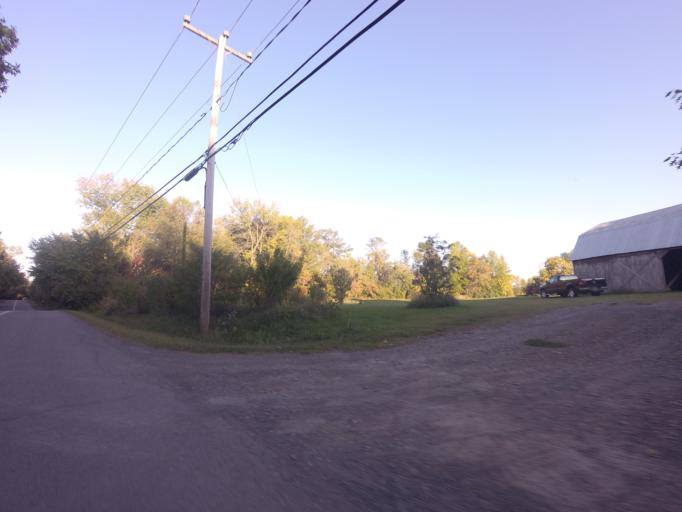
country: CA
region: Quebec
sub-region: Monteregie
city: Rigaud
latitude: 45.4787
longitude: -74.2294
